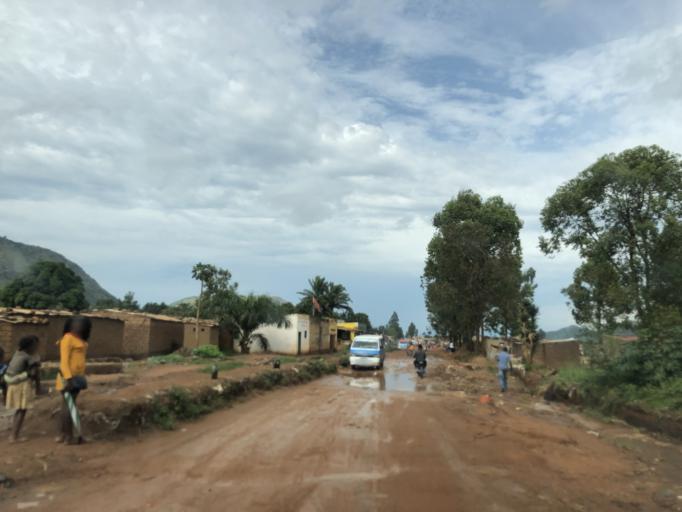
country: AO
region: Cuanza Sul
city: Uacu Cungo
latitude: -11.3484
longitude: 15.0980
